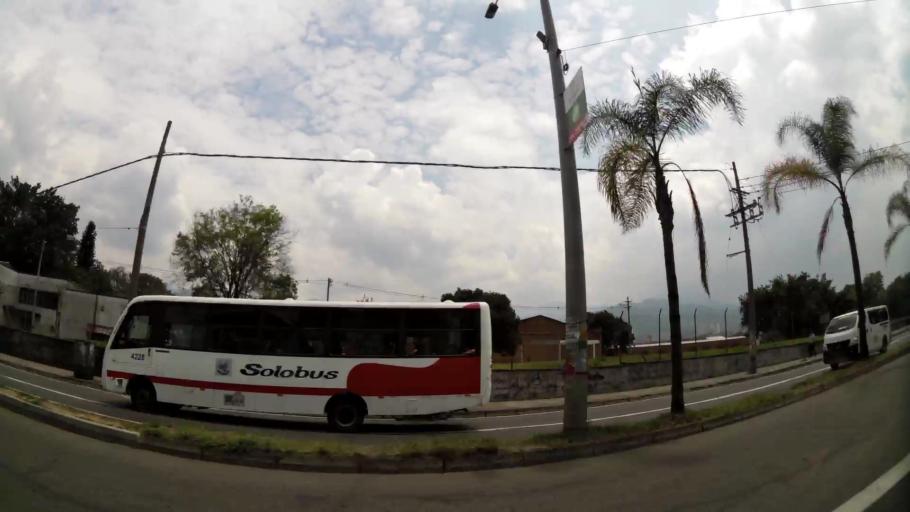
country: CO
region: Antioquia
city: Itagui
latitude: 6.1763
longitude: -75.6041
